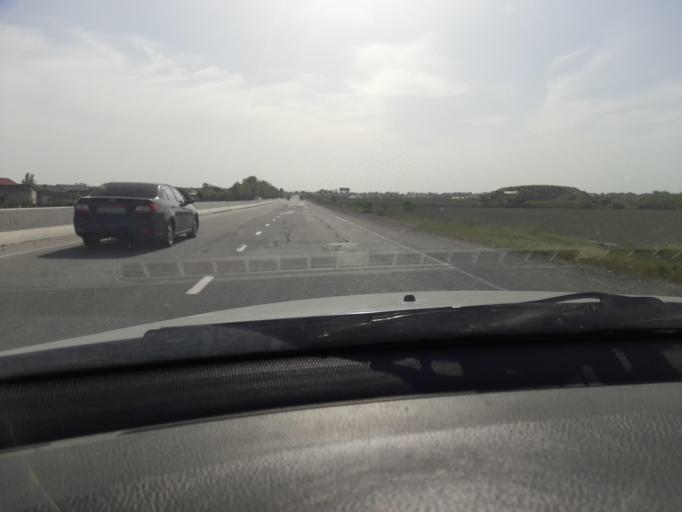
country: UZ
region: Samarqand
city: Kattaqo'rg'on
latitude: 39.9195
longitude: 66.3393
